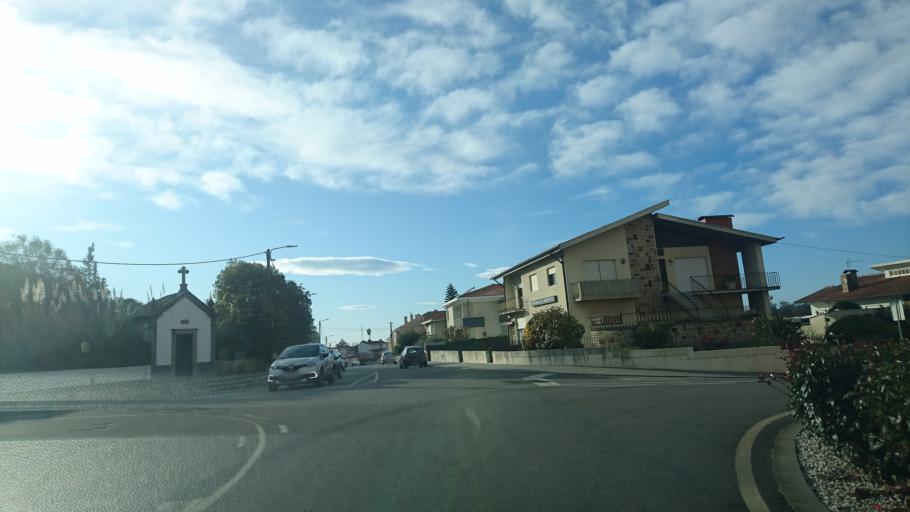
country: PT
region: Aveiro
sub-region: Santa Maria da Feira
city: Pacos de Brandao
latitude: 40.9712
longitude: -8.5907
